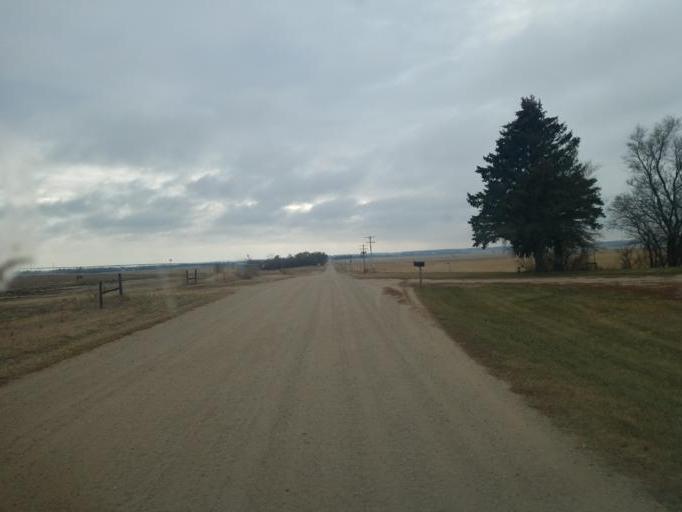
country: US
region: Nebraska
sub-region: Pierce County
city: Plainview
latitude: 42.3845
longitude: -97.7960
